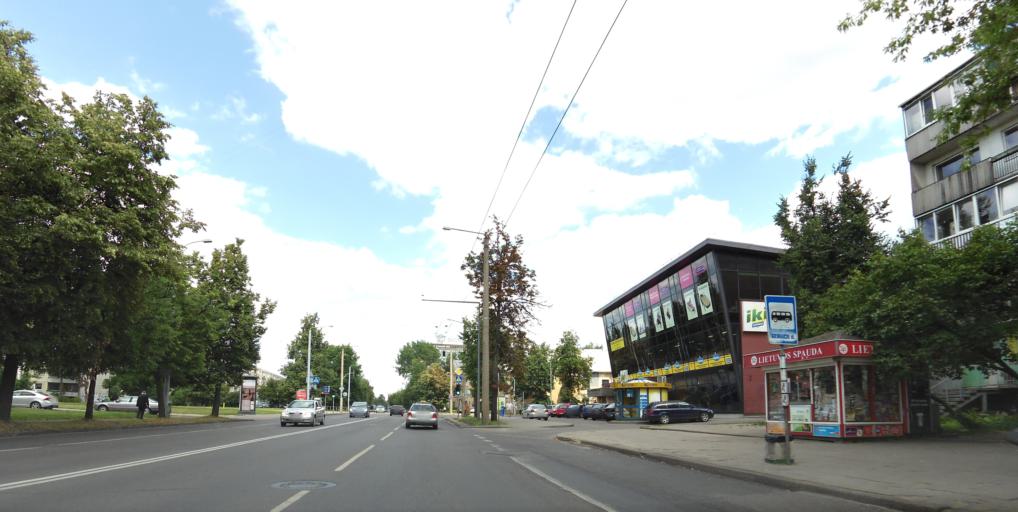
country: LT
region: Vilnius County
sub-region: Vilnius
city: Vilnius
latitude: 54.7080
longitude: 25.2854
